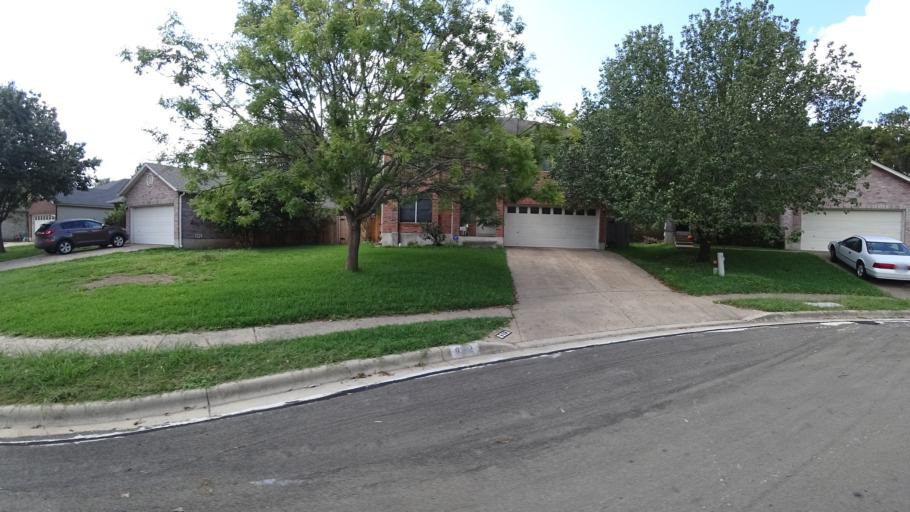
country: US
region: Texas
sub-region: Travis County
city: Manchaca
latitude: 30.1884
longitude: -97.8137
